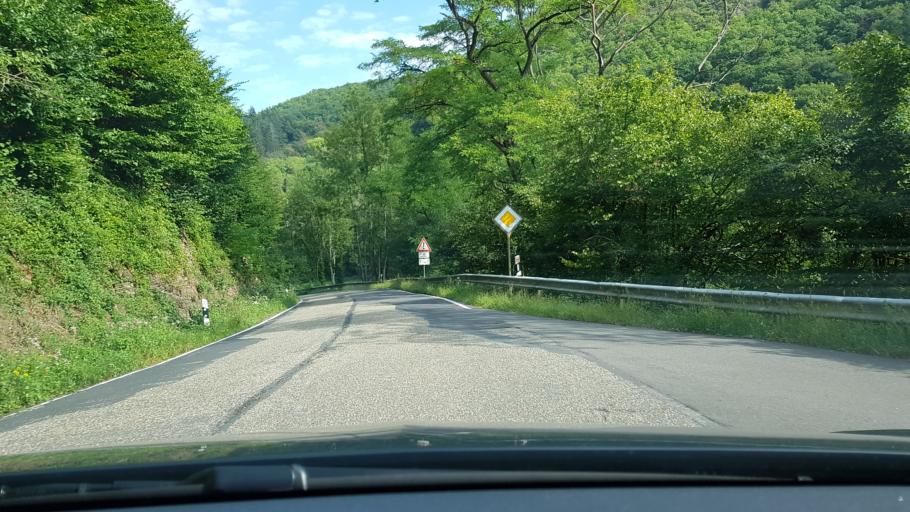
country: DE
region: Rheinland-Pfalz
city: Brodenbach
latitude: 50.2163
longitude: 7.4499
